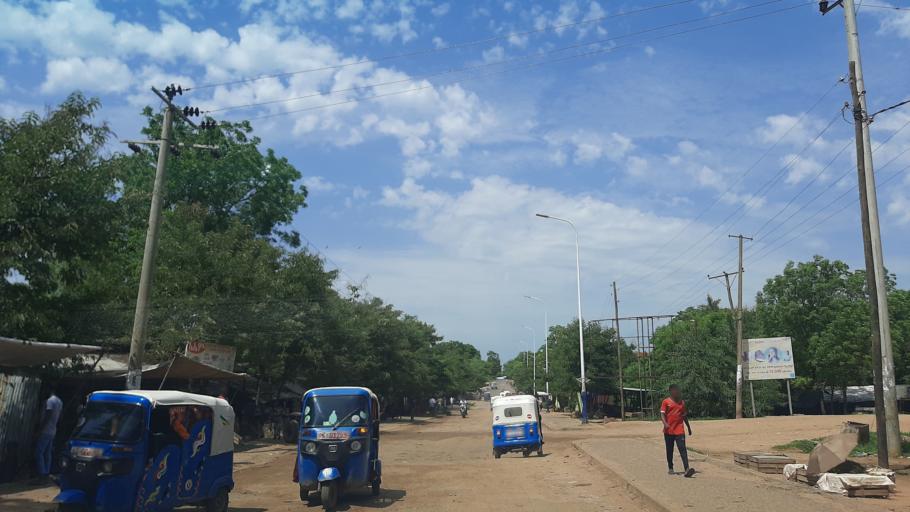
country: ET
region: Gambela
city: Gambela
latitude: 8.2351
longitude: 34.5829
